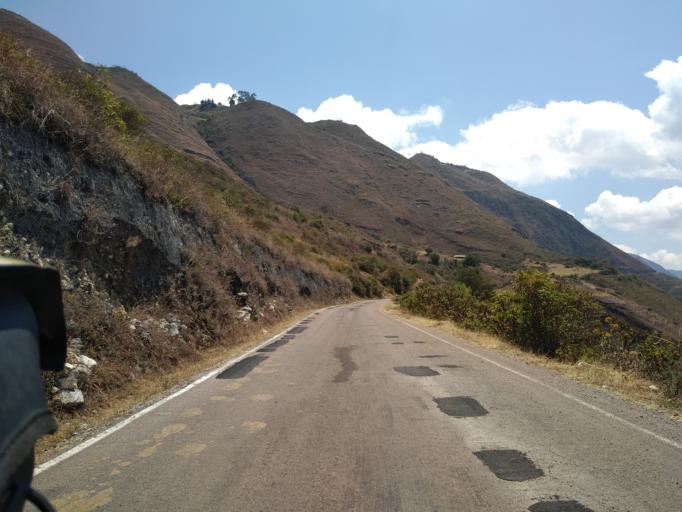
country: PE
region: Cajamarca
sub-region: Provincia de Celendin
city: Celendin
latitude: -6.8827
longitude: -78.1028
